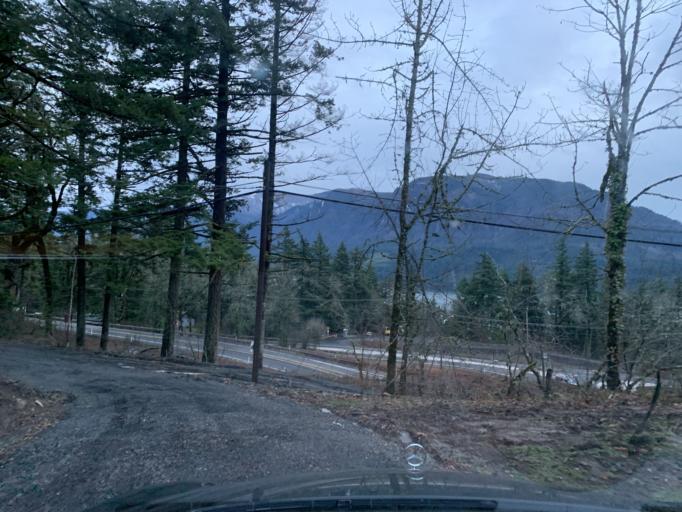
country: US
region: Washington
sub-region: Skamania County
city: Carson
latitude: 45.7159
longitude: -121.8297
